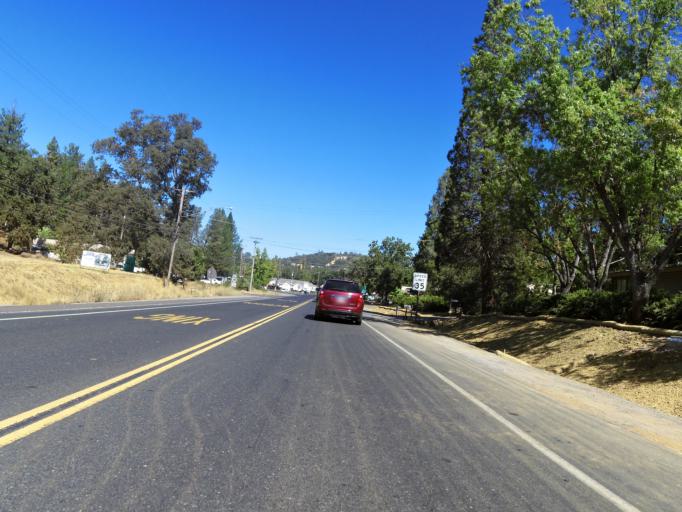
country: US
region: California
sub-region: Calaveras County
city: Murphys
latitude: 38.1347
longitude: -120.4558
